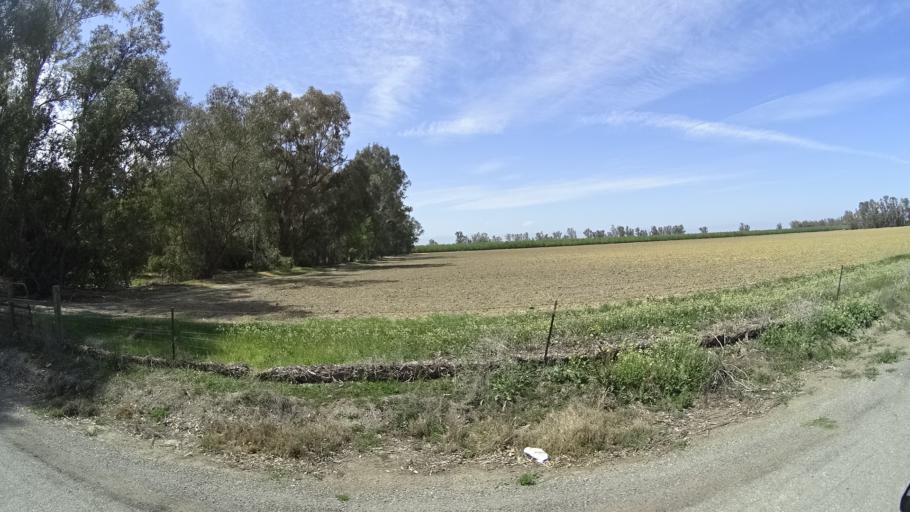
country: US
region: California
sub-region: Glenn County
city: Willows
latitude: 39.5832
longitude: -122.2012
